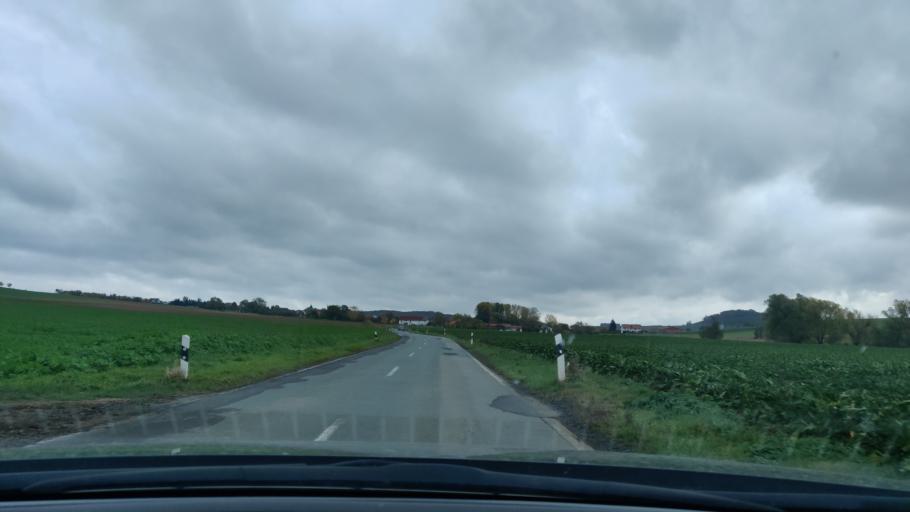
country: DE
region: Hesse
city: Niedenstein
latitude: 51.1860
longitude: 9.3056
